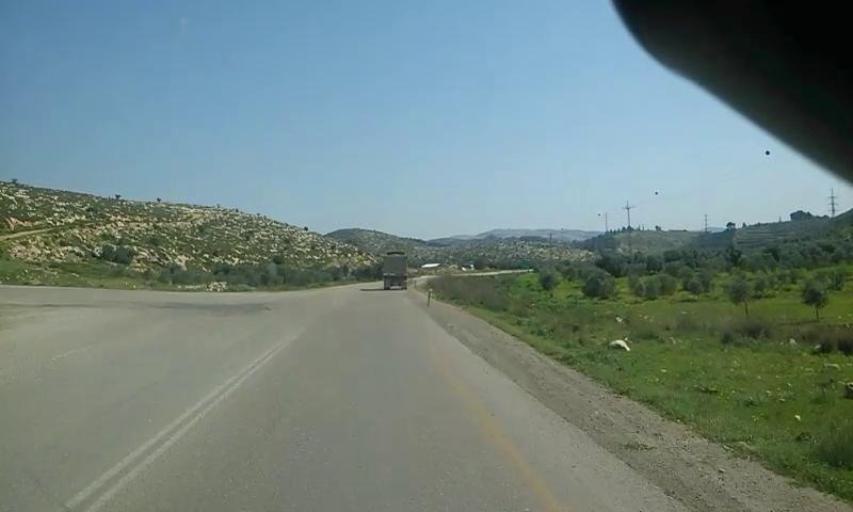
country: PS
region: West Bank
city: Idhna
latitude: 31.5872
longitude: 34.9719
